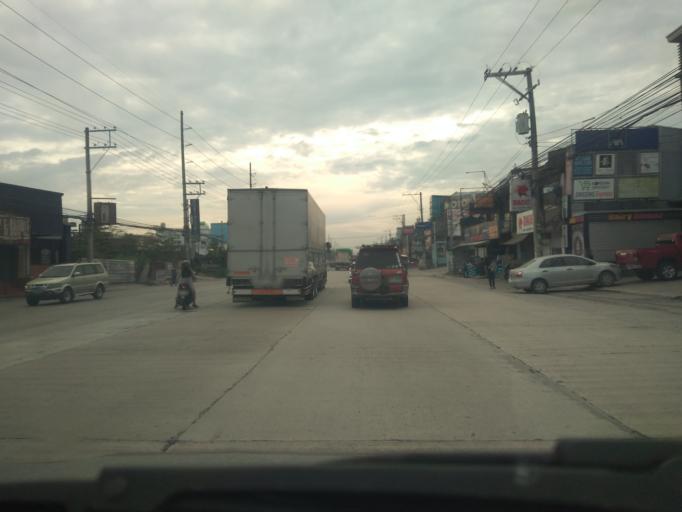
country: PH
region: Central Luzon
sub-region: Province of Pampanga
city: Magliman
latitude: 15.0444
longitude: 120.6731
